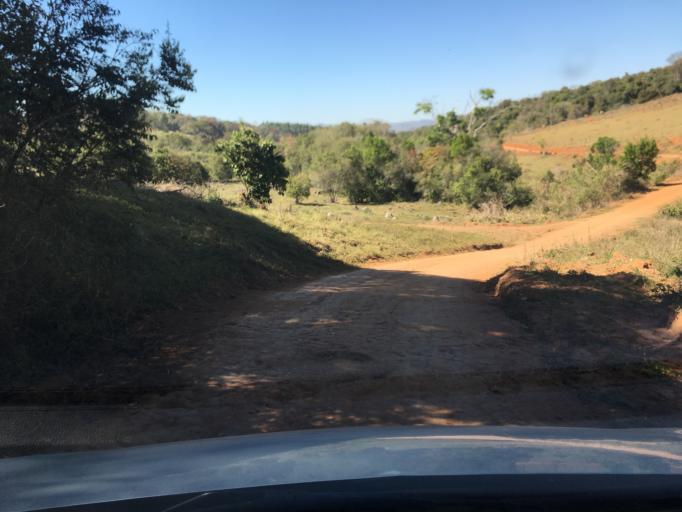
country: BR
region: Minas Gerais
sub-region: Campestre
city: Campestre
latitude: -21.5950
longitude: -46.2061
